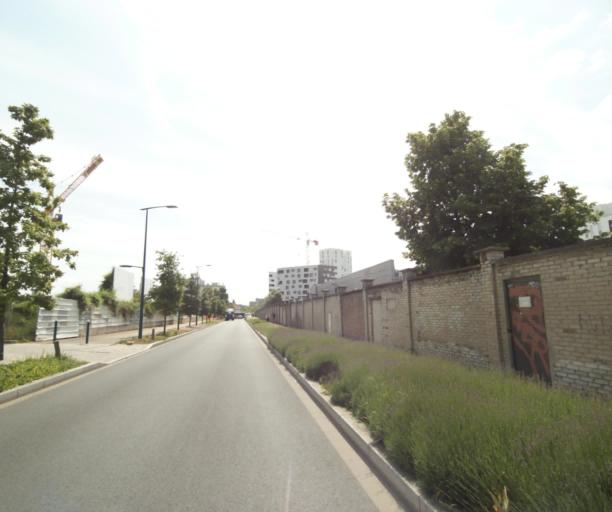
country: FR
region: Ile-de-France
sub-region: Departement des Hauts-de-Seine
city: Villeneuve-la-Garenne
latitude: 48.9216
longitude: 2.3157
